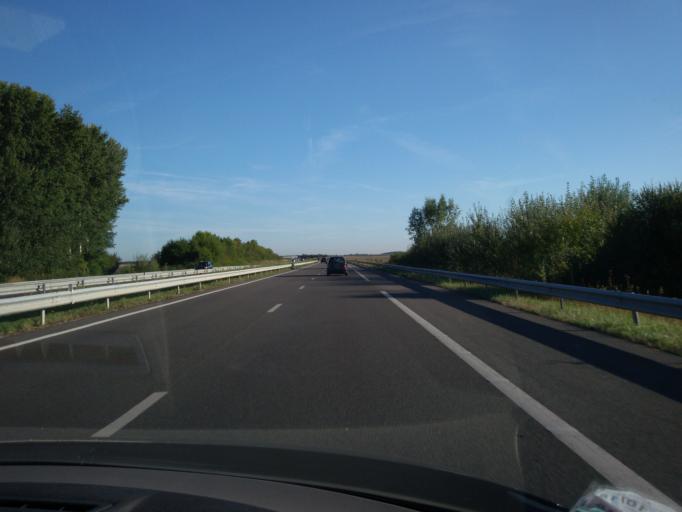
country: FR
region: Centre
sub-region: Departement du Cher
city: Chateauneuf-sur-Cher
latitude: 46.8163
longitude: 2.4129
